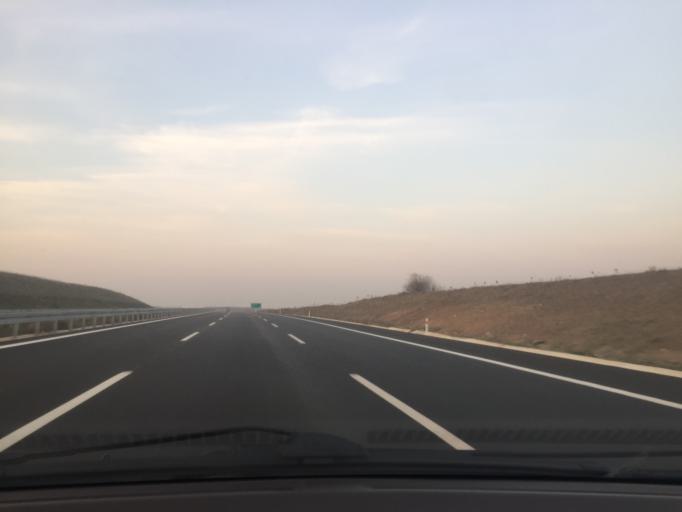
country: TR
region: Bursa
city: Karacabey
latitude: 40.2705
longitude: 28.4993
